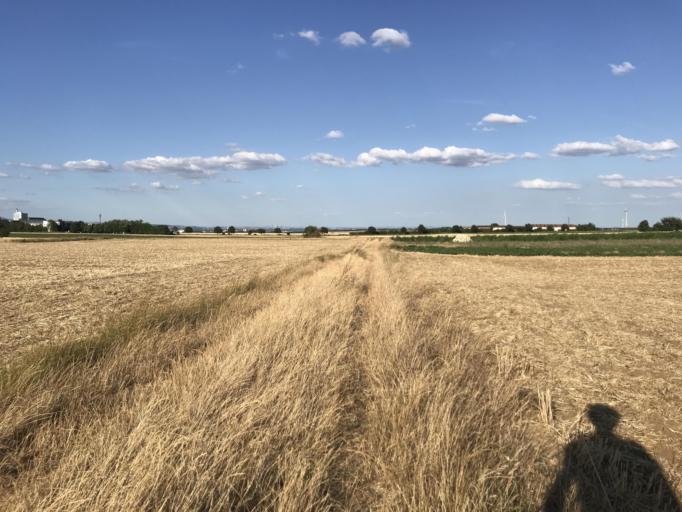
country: DE
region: Rheinland-Pfalz
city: Ober-Olm
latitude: 49.9455
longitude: 8.1835
